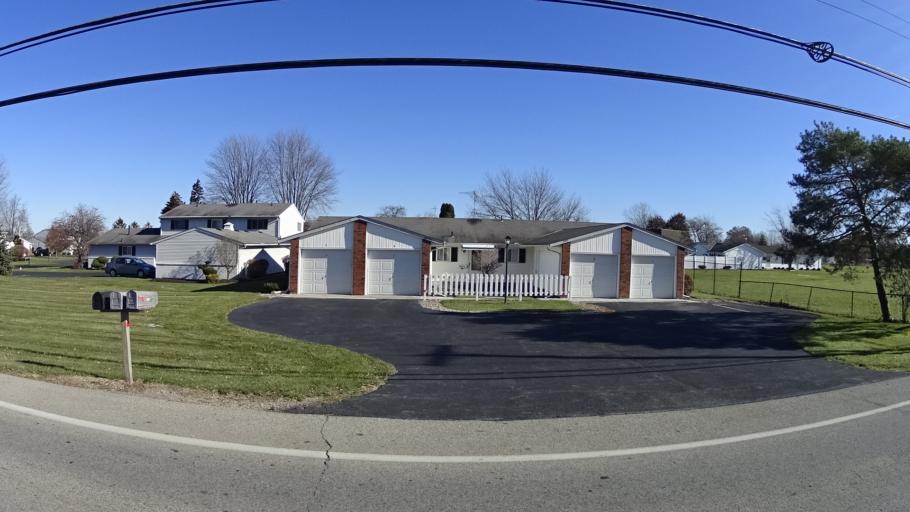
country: US
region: Ohio
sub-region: Lorain County
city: Elyria
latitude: 41.3600
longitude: -82.1576
